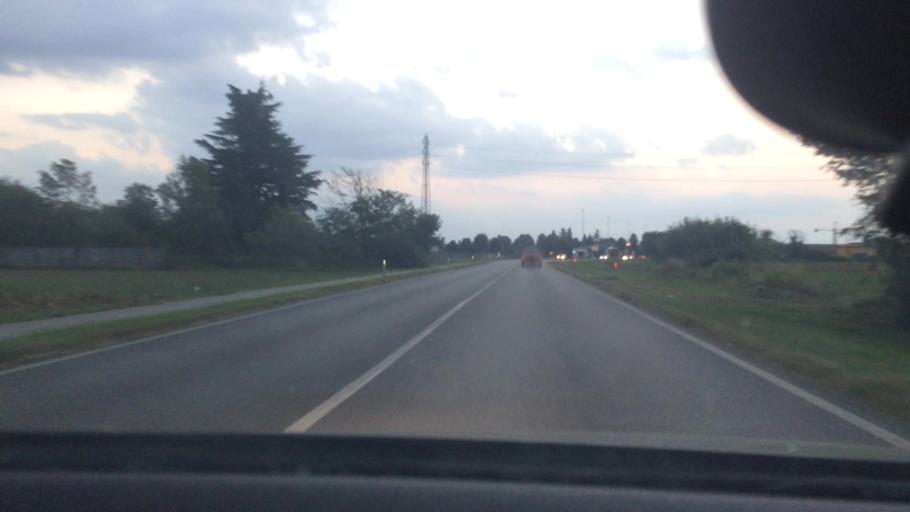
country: IT
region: Lombardy
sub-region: Citta metropolitana di Milano
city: Buscate
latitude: 45.5463
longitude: 8.7980
